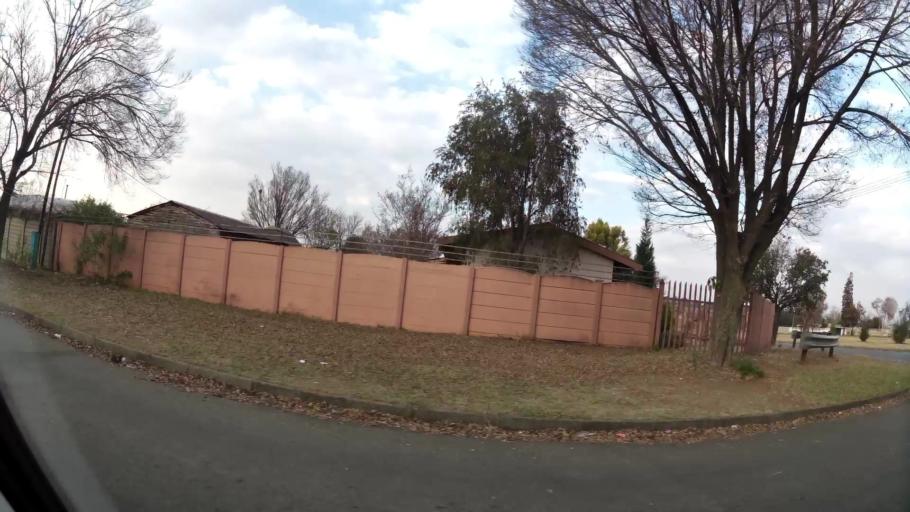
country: ZA
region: Gauteng
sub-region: Ekurhuleni Metropolitan Municipality
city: Germiston
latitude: -26.2359
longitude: 28.1992
